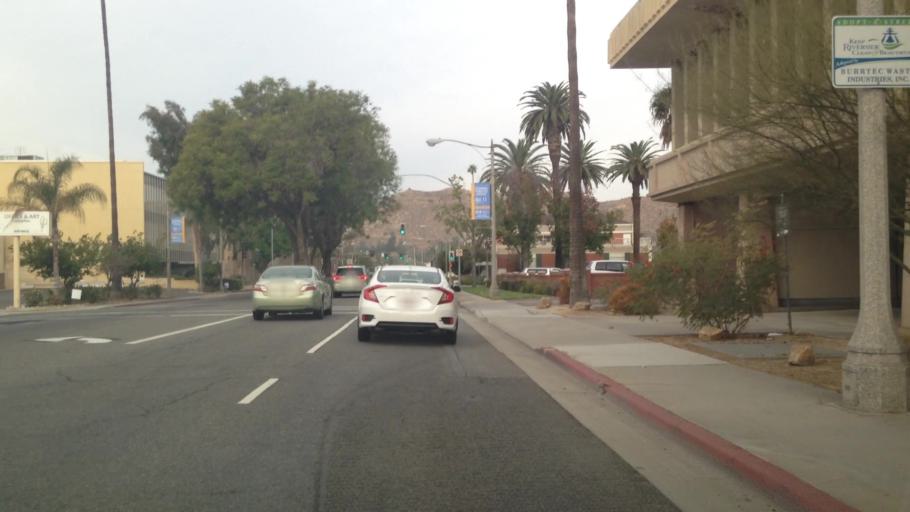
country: US
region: California
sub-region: Riverside County
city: Riverside
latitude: 33.9752
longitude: -117.3761
